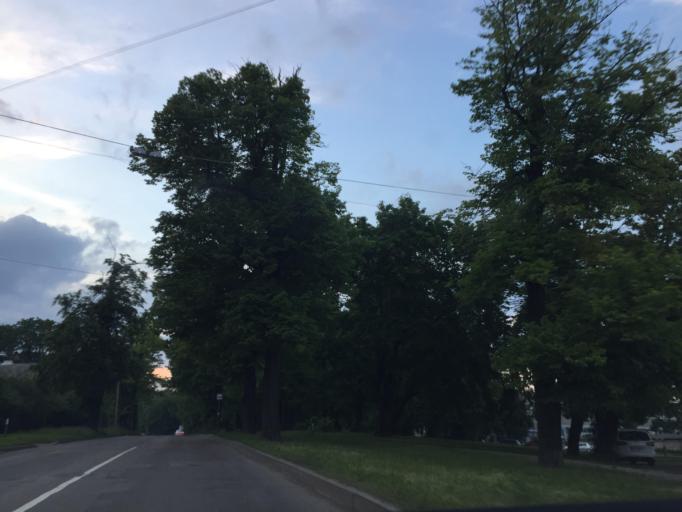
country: LV
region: Riga
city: Riga
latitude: 56.9719
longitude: 24.0639
